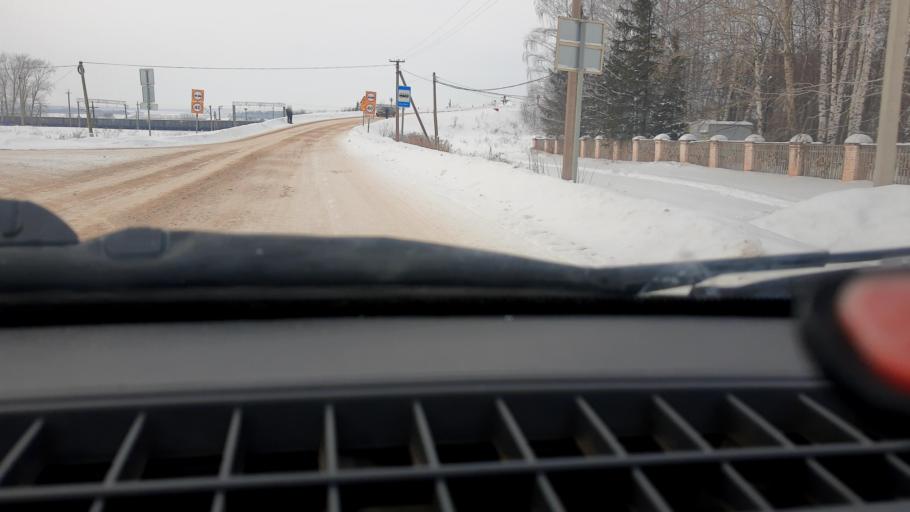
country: RU
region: Bashkortostan
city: Davlekanovo
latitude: 54.5804
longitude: 54.9340
